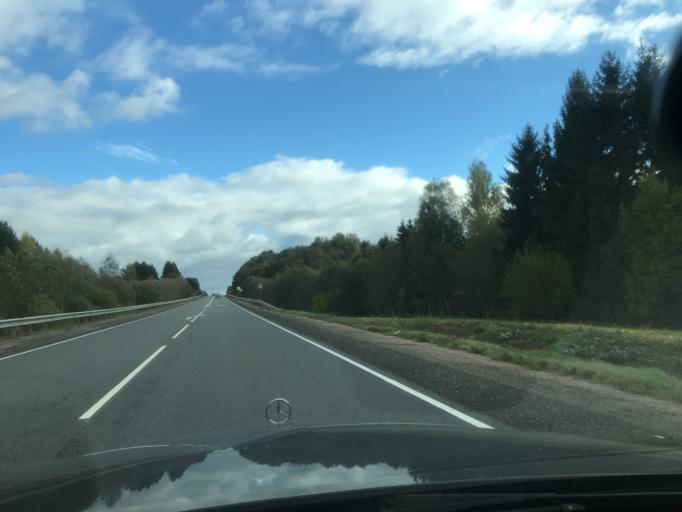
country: RU
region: Pskov
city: Opochka
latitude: 56.6469
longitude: 28.7739
